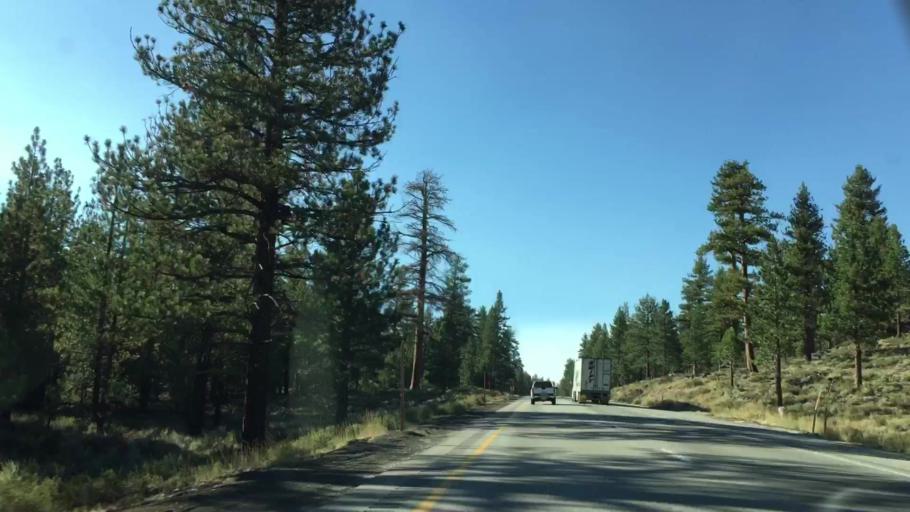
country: US
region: California
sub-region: Mono County
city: Mammoth Lakes
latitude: 37.6693
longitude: -118.9343
